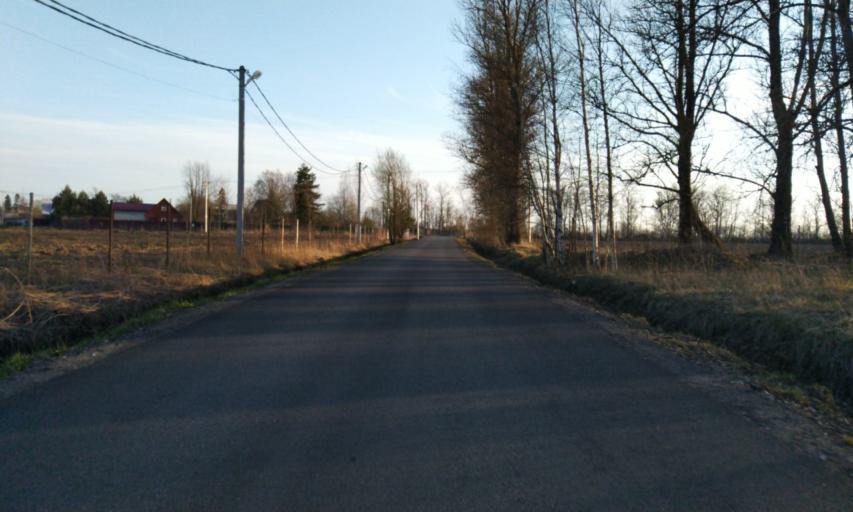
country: RU
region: Leningrad
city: Novoye Devyatkino
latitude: 60.1036
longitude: 30.4493
